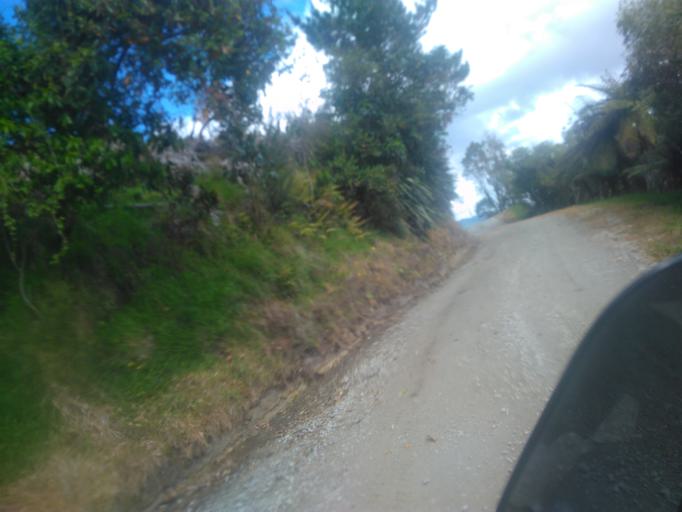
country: NZ
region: Hawke's Bay
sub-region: Wairoa District
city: Wairoa
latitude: -38.7757
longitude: 177.6265
